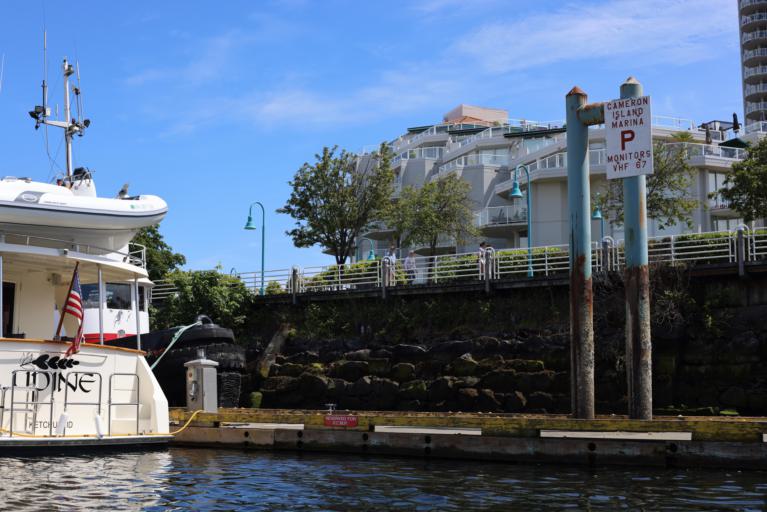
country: CA
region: British Columbia
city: Nanaimo
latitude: 49.1672
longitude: -123.9339
